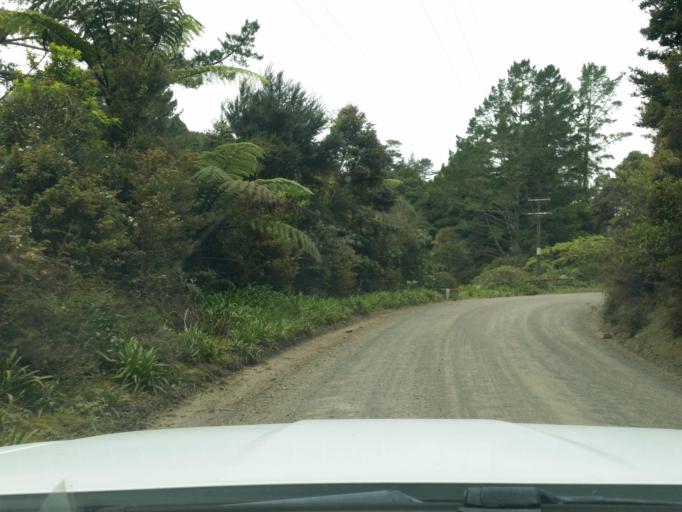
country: NZ
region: Northland
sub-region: Kaipara District
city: Dargaville
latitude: -35.7123
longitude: 173.6274
